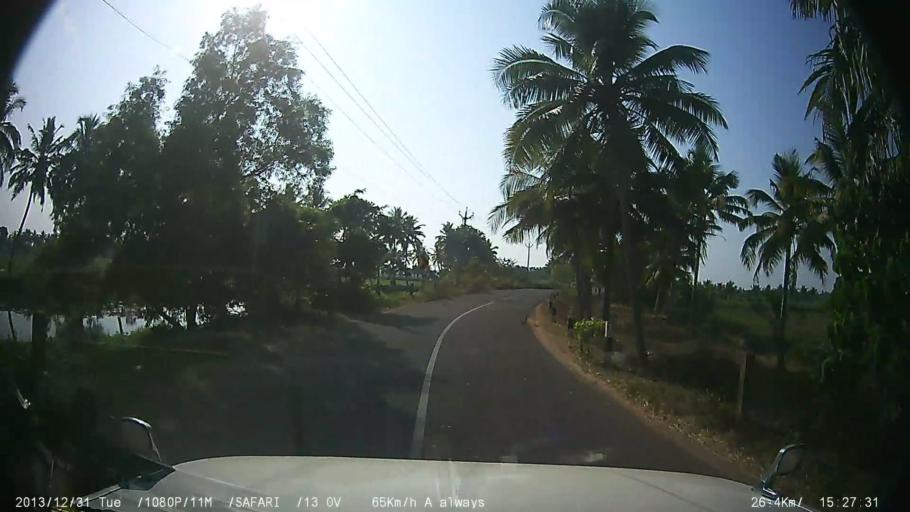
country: IN
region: Kerala
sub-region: Kottayam
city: Vaikam
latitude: 9.6832
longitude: 76.4501
